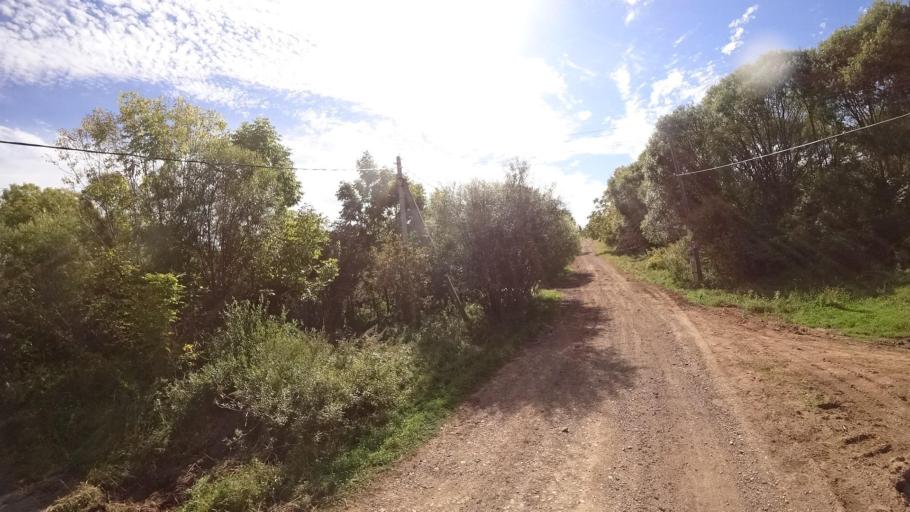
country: RU
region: Primorskiy
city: Yakovlevka
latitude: 44.3907
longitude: 133.6076
